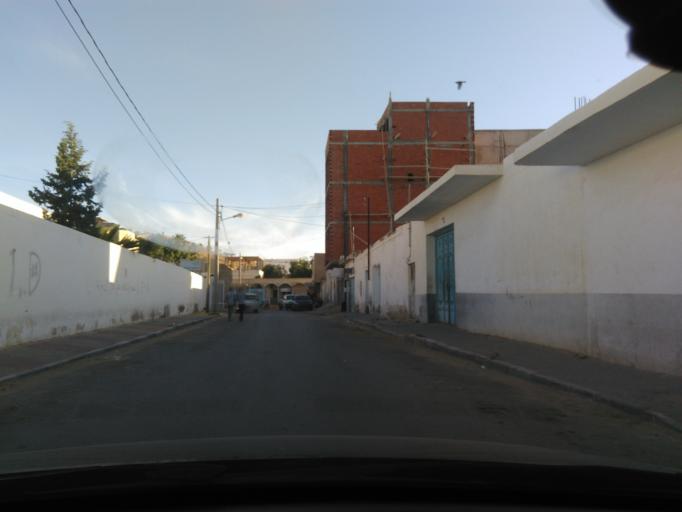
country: TN
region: Tataouine
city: Tataouine
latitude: 32.9300
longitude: 10.4486
